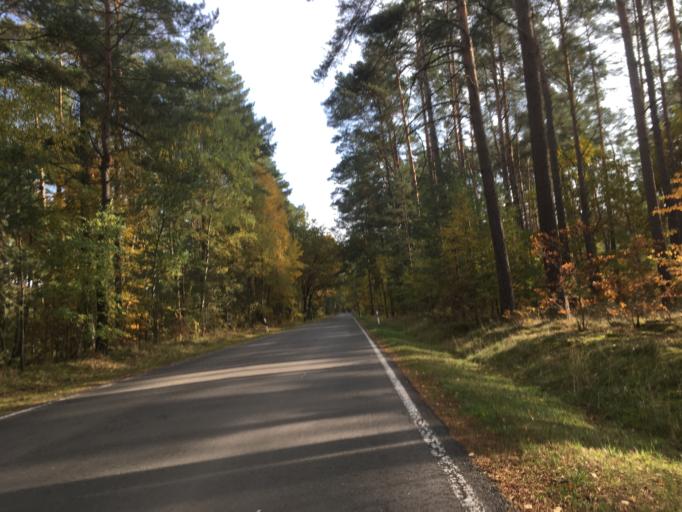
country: DE
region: Brandenburg
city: Templin
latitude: 53.0395
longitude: 13.4612
